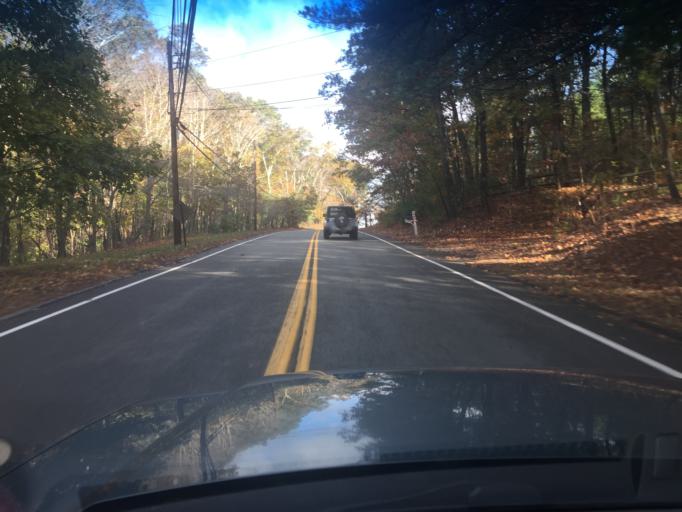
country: US
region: Massachusetts
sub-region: Norfolk County
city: Medfield
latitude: 42.2181
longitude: -71.3029
